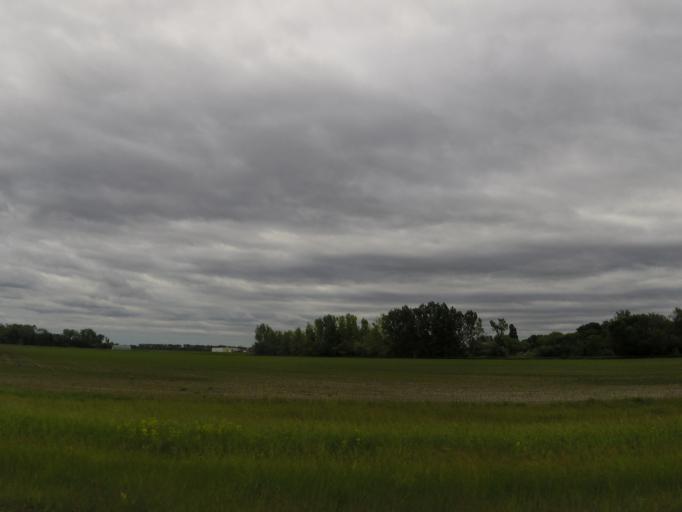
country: US
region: North Dakota
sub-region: Walsh County
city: Grafton
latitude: 48.5091
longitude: -97.4435
